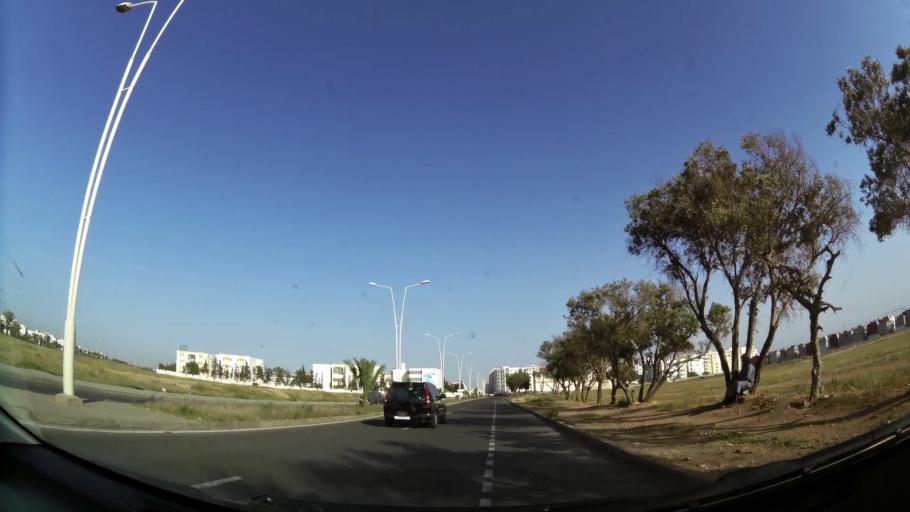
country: MA
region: Oued ed Dahab-Lagouira
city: Dakhla
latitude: 30.4029
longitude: -9.5581
